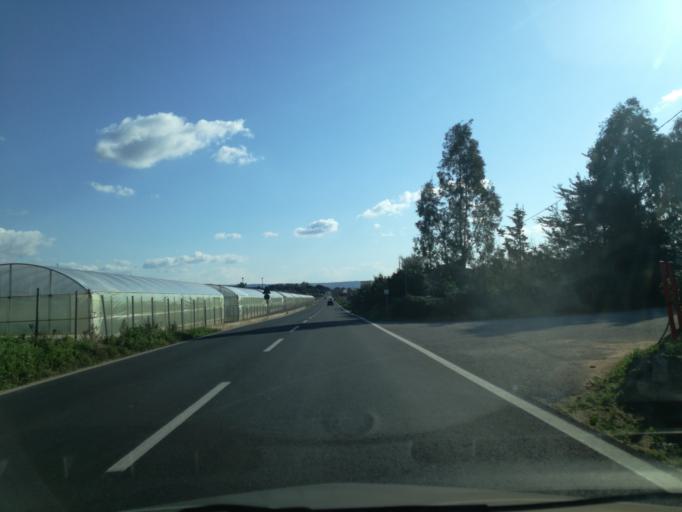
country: IT
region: Sicily
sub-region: Ragusa
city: Vittoria
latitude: 36.9686
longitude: 14.4808
